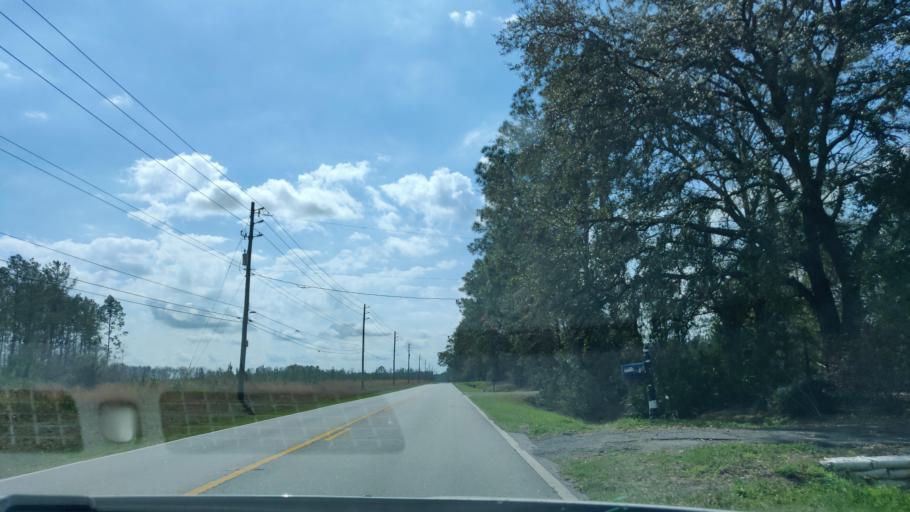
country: US
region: Florida
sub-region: Duval County
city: Baldwin
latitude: 30.2388
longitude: -81.9410
